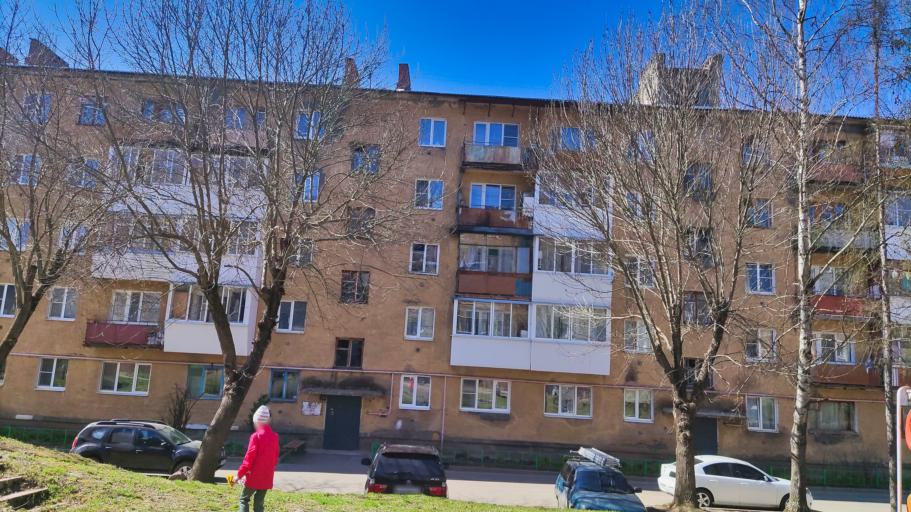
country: RU
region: Tverskaya
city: Rzhev
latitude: 56.2580
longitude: 34.3448
